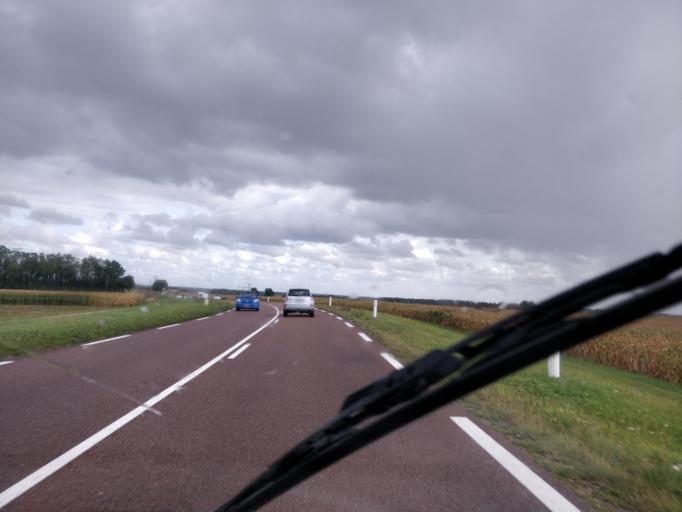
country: FR
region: Champagne-Ardenne
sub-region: Departement de l'Aube
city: Verrieres
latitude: 48.2775
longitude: 4.1979
